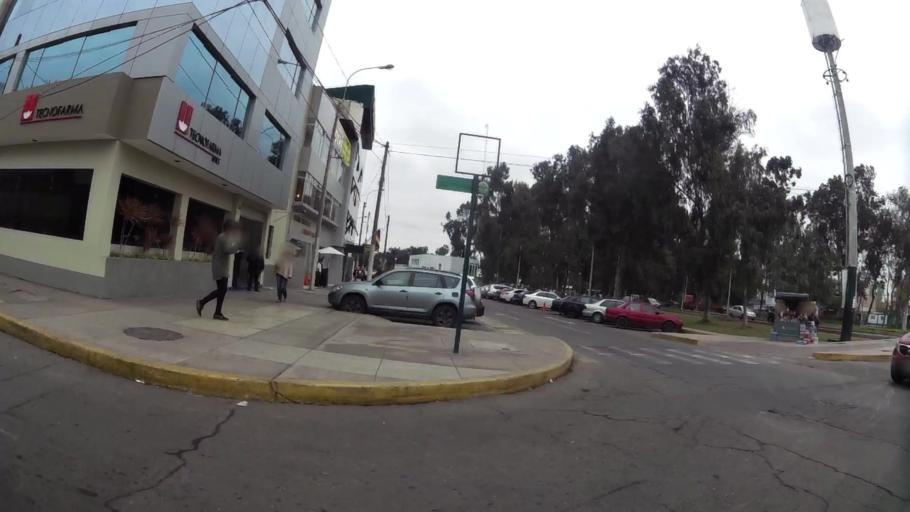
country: PE
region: Lima
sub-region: Lima
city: La Molina
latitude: -12.0711
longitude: -76.9548
